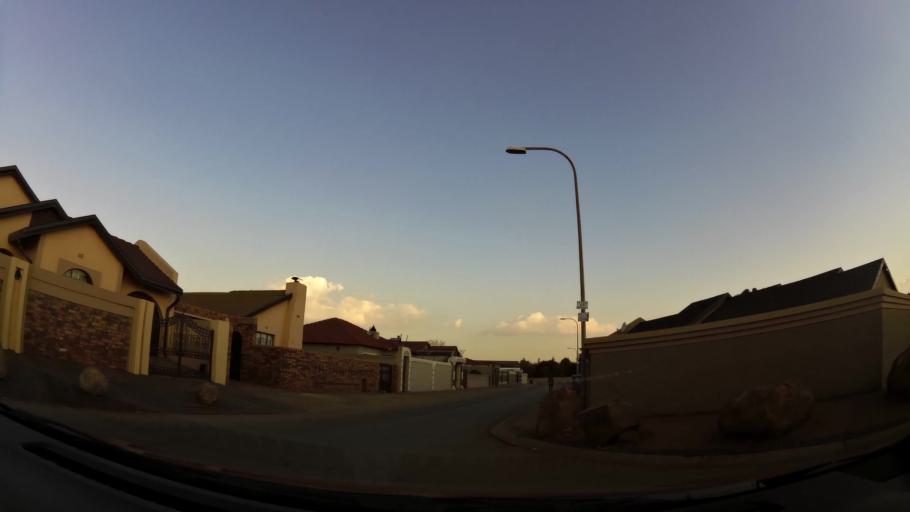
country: ZA
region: Gauteng
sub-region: City of Johannesburg Metropolitan Municipality
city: Soweto
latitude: -26.2196
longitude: 27.8561
